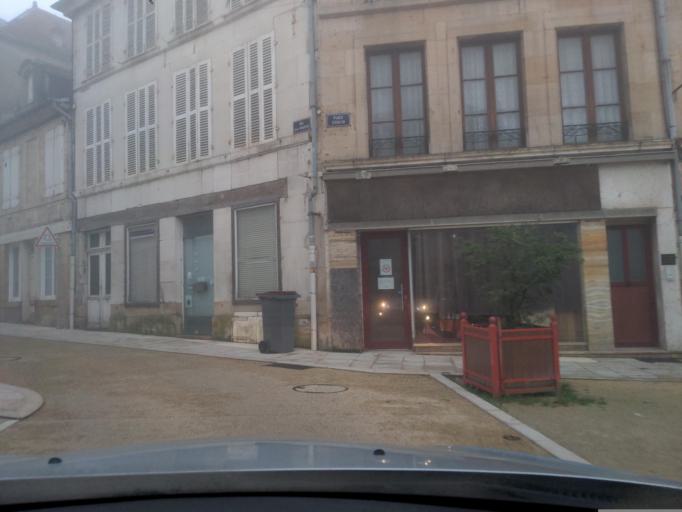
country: FR
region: Champagne-Ardenne
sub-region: Departement de la Haute-Marne
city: Langres
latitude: 47.8633
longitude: 5.3325
